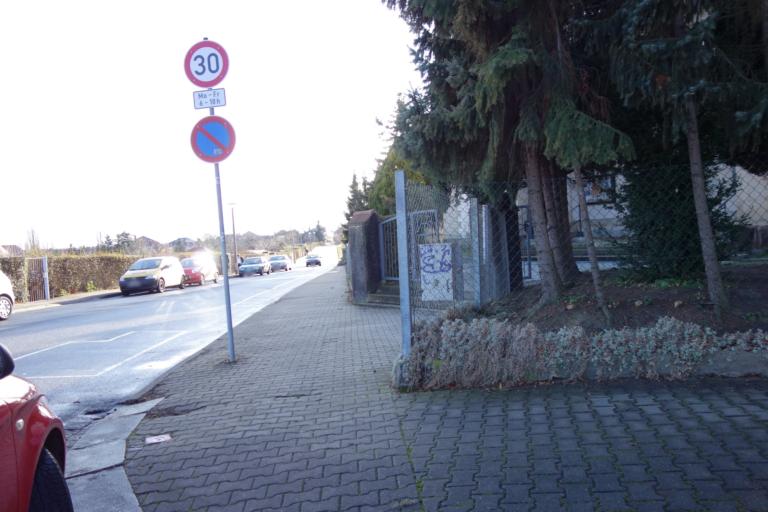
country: DE
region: Saxony
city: Radebeul
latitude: 51.0567
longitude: 13.6784
